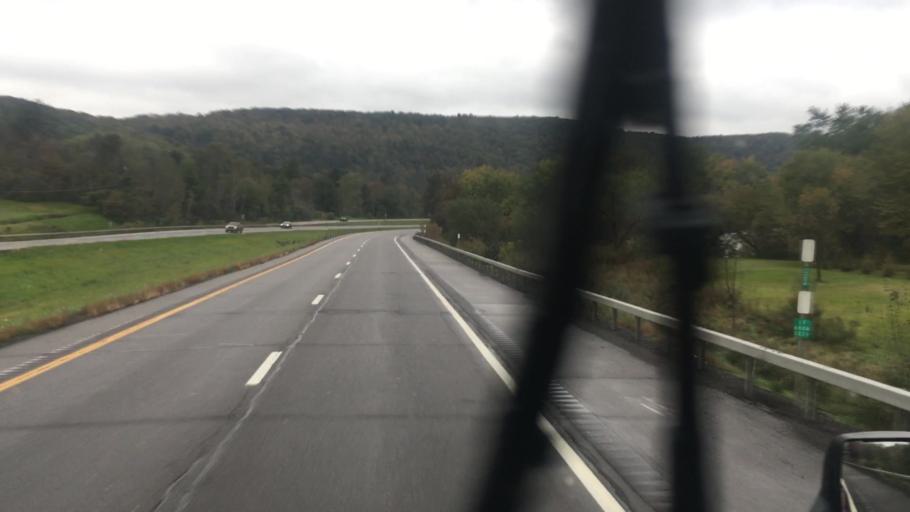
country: US
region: New York
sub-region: Tioga County
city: Apalachin
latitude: 42.0813
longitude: -76.2037
